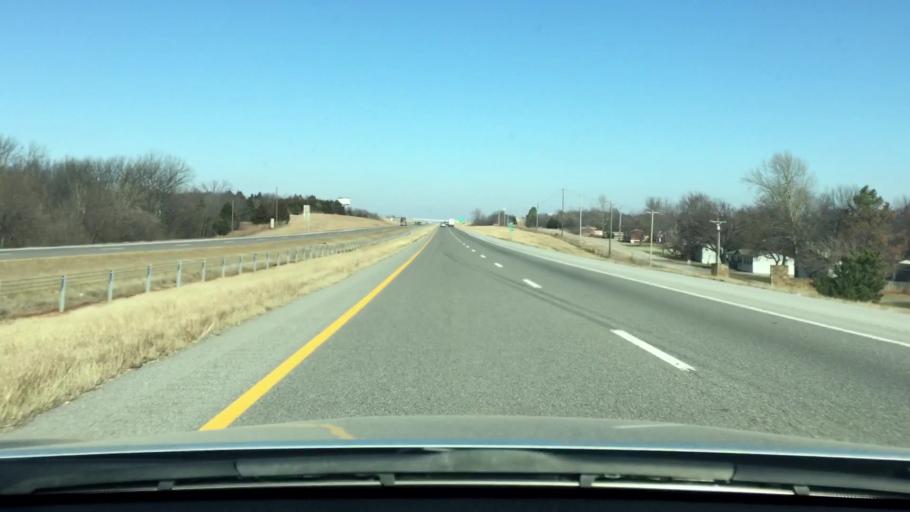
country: US
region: Oklahoma
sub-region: McClain County
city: Purcell
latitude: 34.9704
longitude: -97.3707
